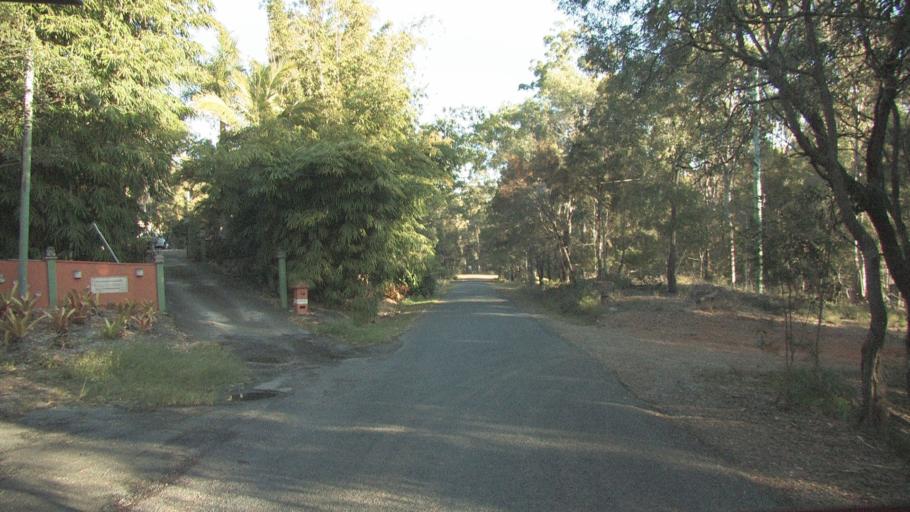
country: AU
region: Queensland
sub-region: Logan
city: Windaroo
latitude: -27.7448
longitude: 153.1484
